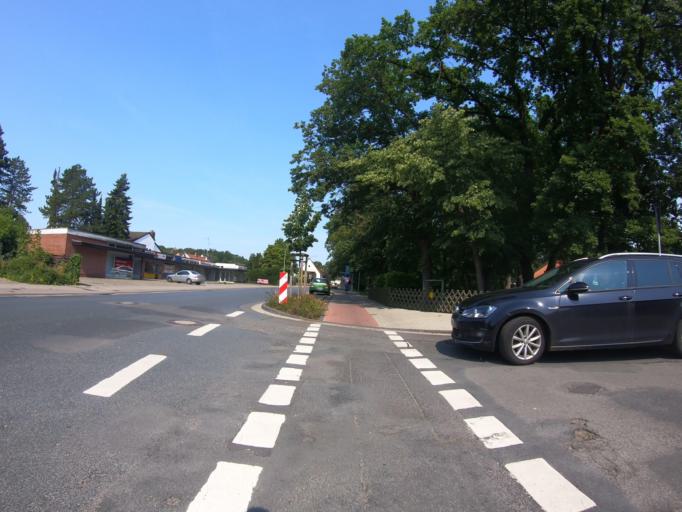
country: DE
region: Lower Saxony
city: Gifhorn
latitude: 52.4759
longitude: 10.5561
